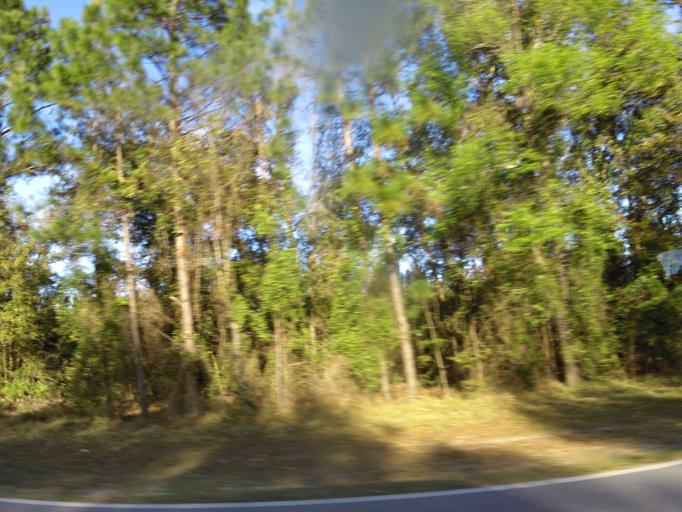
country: US
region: Florida
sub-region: Duval County
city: Jacksonville
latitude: 30.4376
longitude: -81.6045
